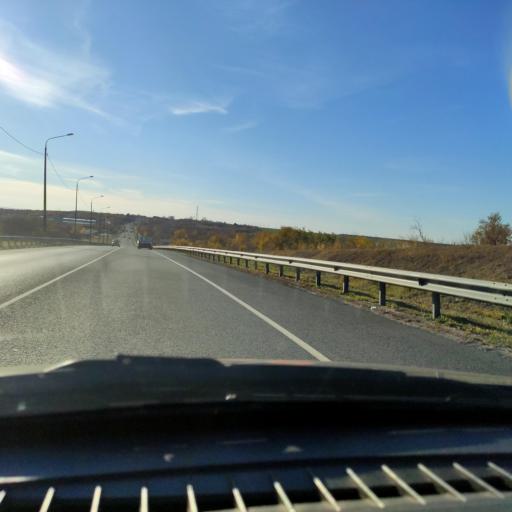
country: RU
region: Samara
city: Mezhdurechensk
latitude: 53.2537
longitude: 49.0387
